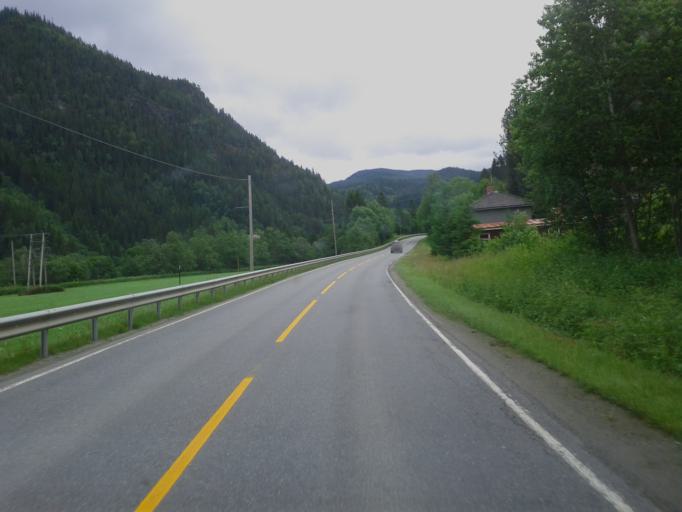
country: NO
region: Sor-Trondelag
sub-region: Midtre Gauldal
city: Storen
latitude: 62.9902
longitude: 10.5342
